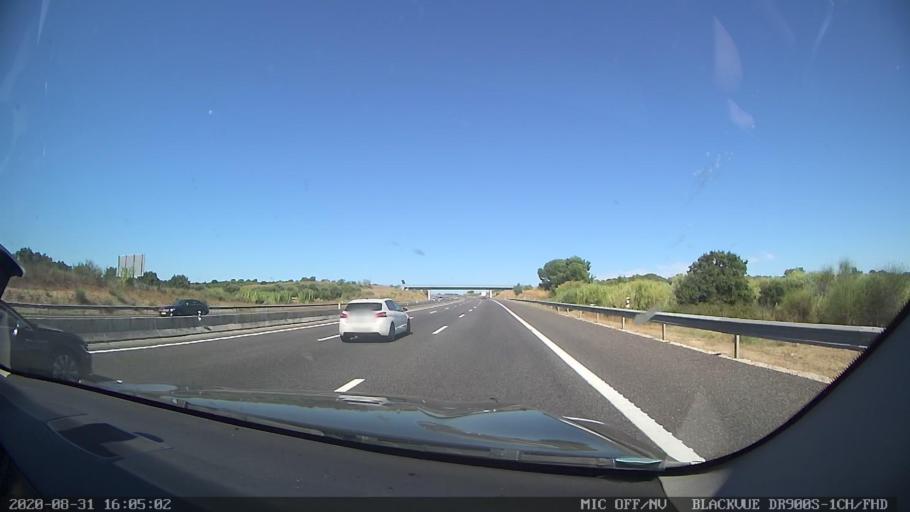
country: PT
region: Santarem
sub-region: Cartaxo
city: Pontevel
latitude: 39.1640
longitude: -8.8584
